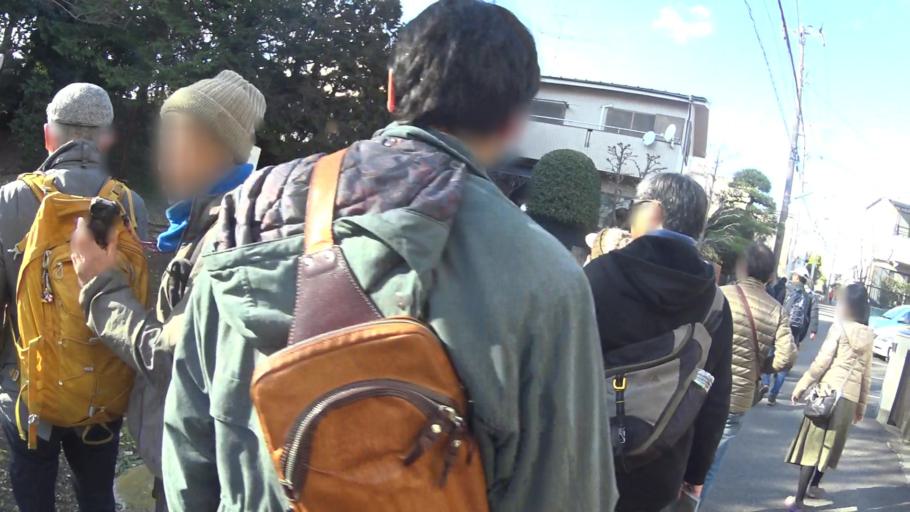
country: JP
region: Tokyo
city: Mitaka-shi
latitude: 35.6538
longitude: 139.6048
